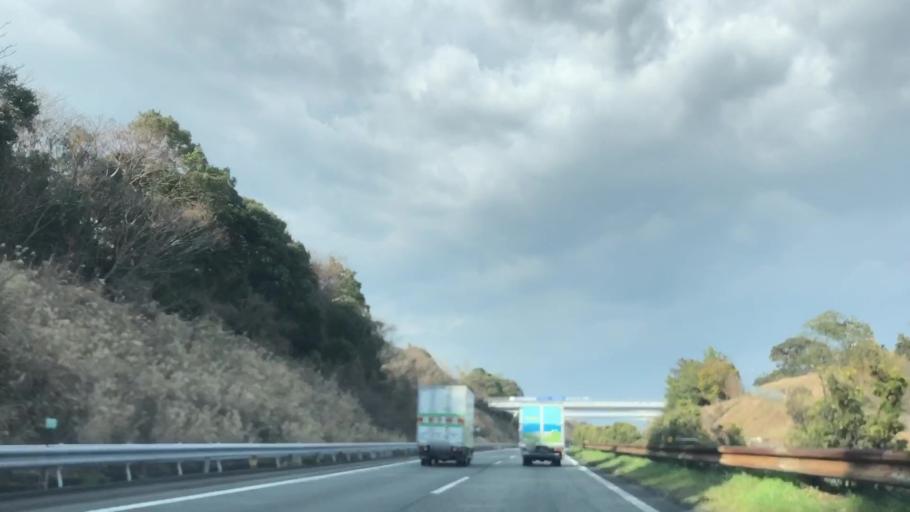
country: JP
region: Shizuoka
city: Shimada
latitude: 34.7825
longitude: 138.2297
